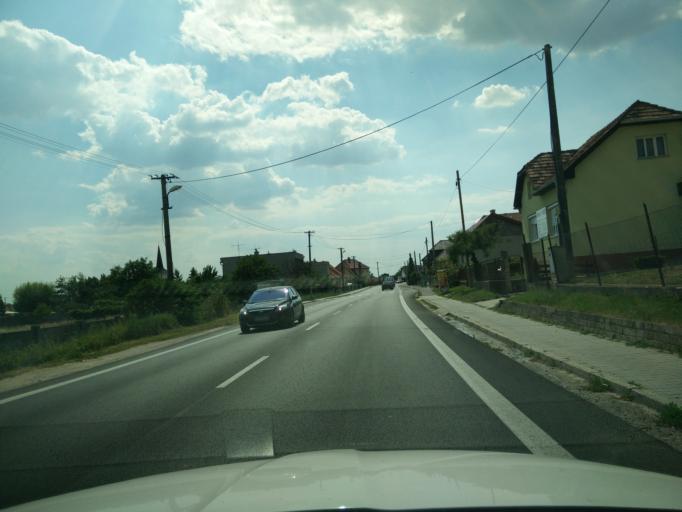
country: SK
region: Nitriansky
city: Partizanske
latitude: 48.6294
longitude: 18.3412
